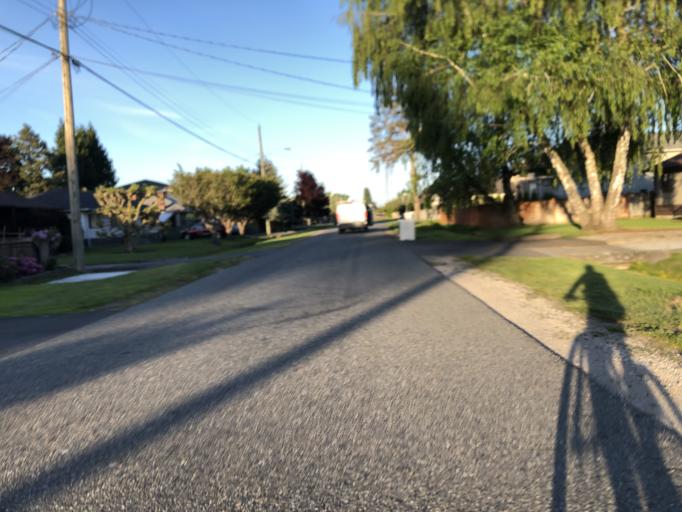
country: CA
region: British Columbia
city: Richmond
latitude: 49.1418
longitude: -123.1326
